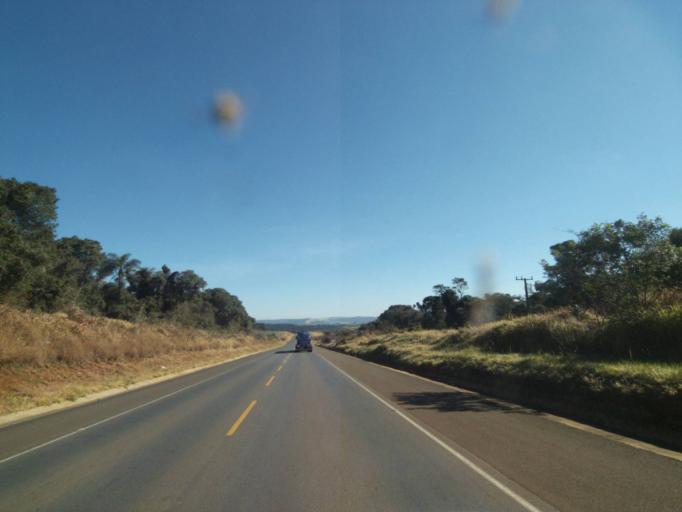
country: BR
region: Parana
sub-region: Tibagi
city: Tibagi
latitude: -24.4614
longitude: -50.4293
